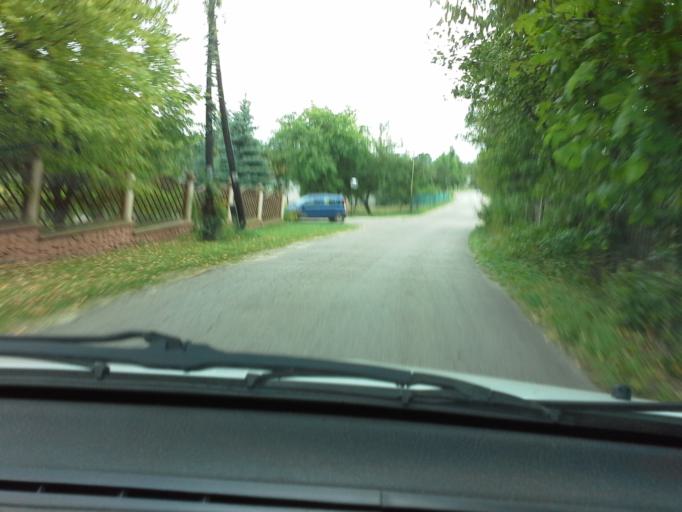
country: PL
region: Lesser Poland Voivodeship
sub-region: Powiat chrzanowski
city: Plaza
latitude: 50.1269
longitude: 19.4526
